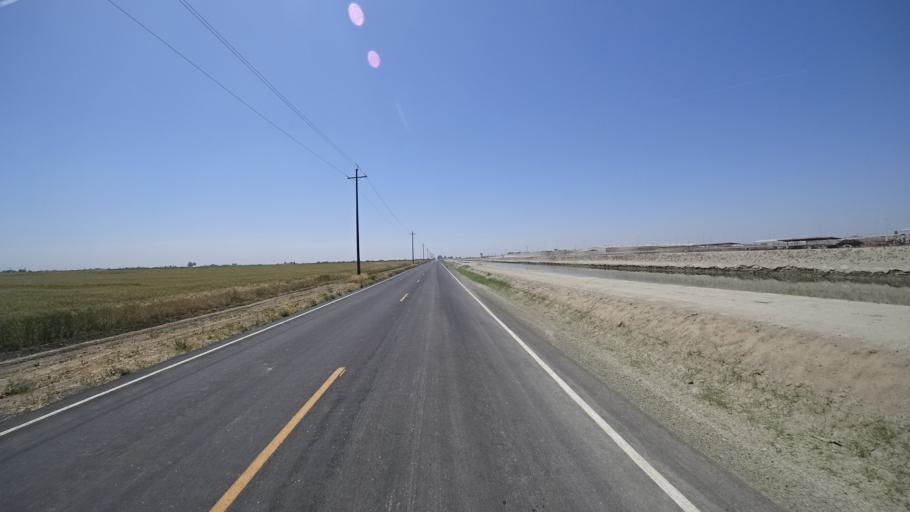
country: US
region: California
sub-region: Kings County
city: Corcoran
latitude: 36.0613
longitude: -119.5363
